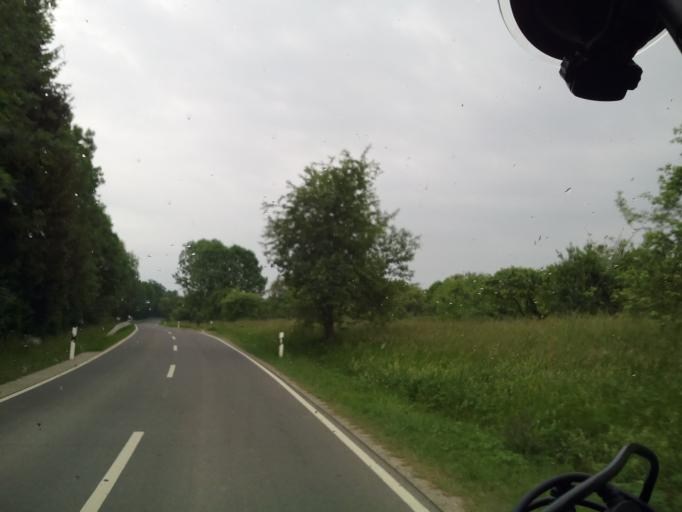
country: DE
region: Bavaria
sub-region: Regierungsbezirk Unterfranken
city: Hochheim
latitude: 50.3862
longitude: 10.4124
